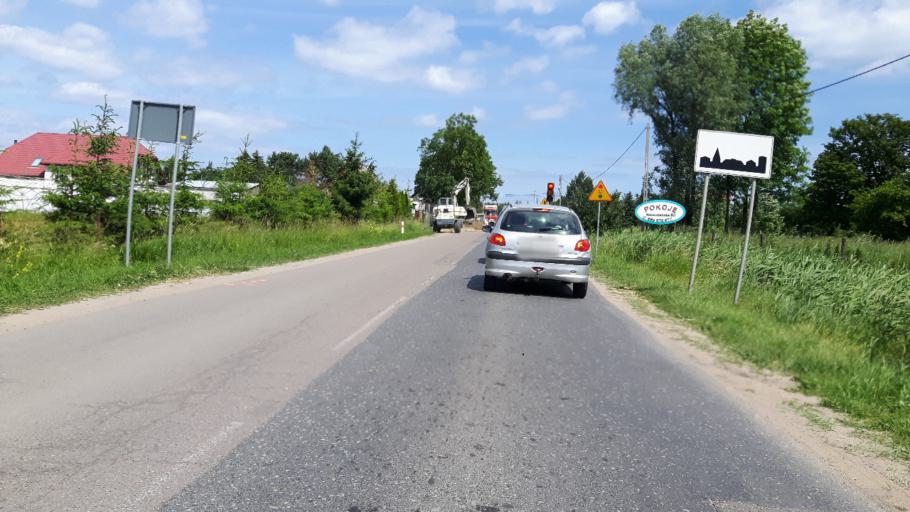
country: PL
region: Pomeranian Voivodeship
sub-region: Powiat gdanski
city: Cedry Wielkie
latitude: 54.3372
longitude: 18.8230
